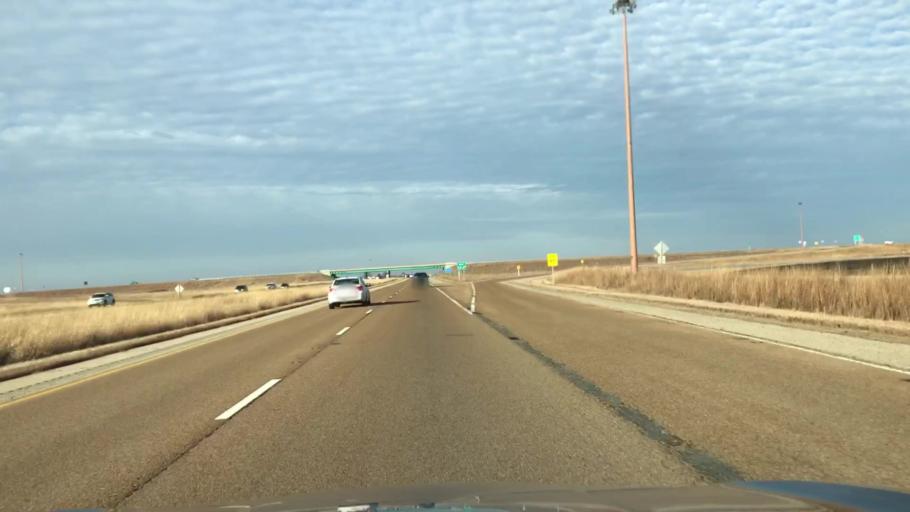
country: US
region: Illinois
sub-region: Montgomery County
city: Raymond
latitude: 39.3175
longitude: -89.6424
